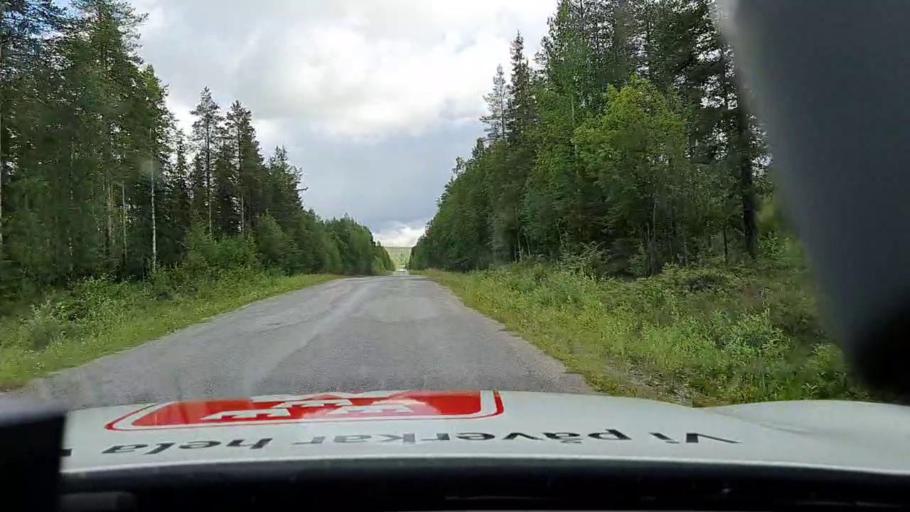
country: SE
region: Norrbotten
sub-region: Overkalix Kommun
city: OEverkalix
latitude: 66.2488
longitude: 23.0087
